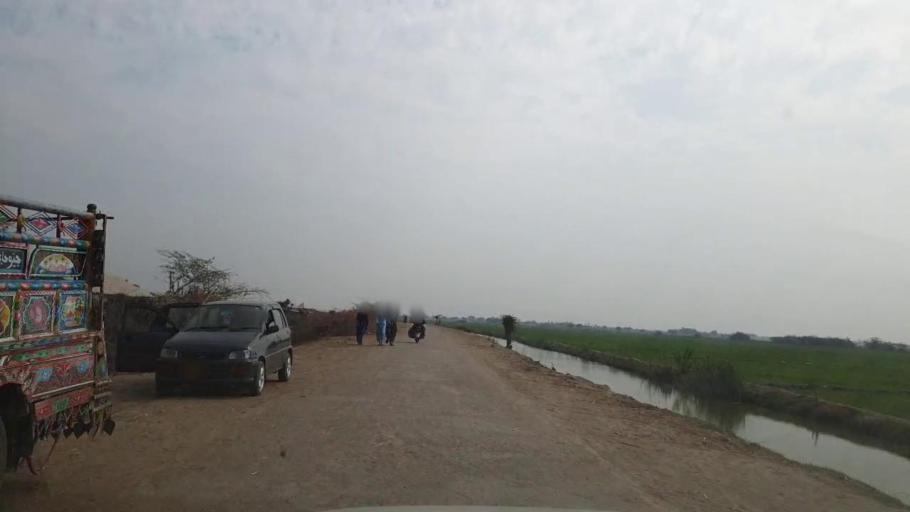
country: PK
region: Sindh
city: Mirpur Khas
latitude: 25.5357
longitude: 69.1312
